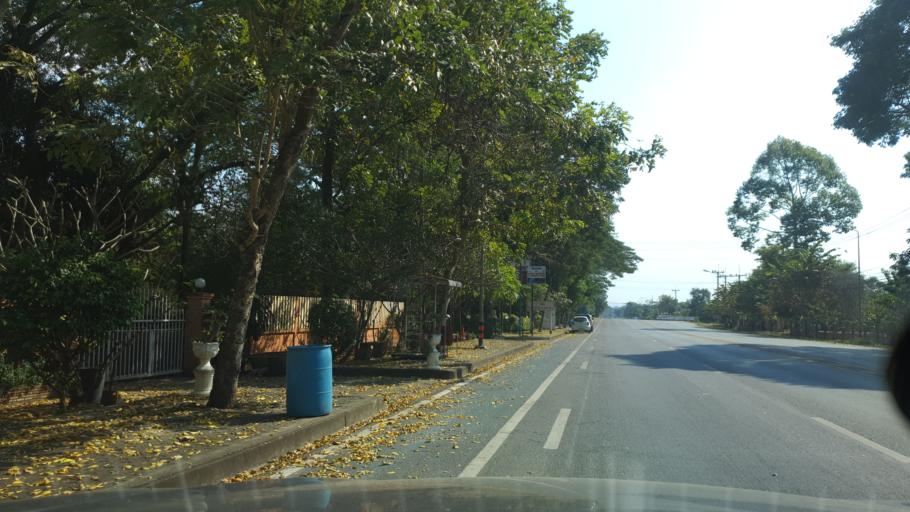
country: TH
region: Tak
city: Tak
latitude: 16.8677
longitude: 99.1195
